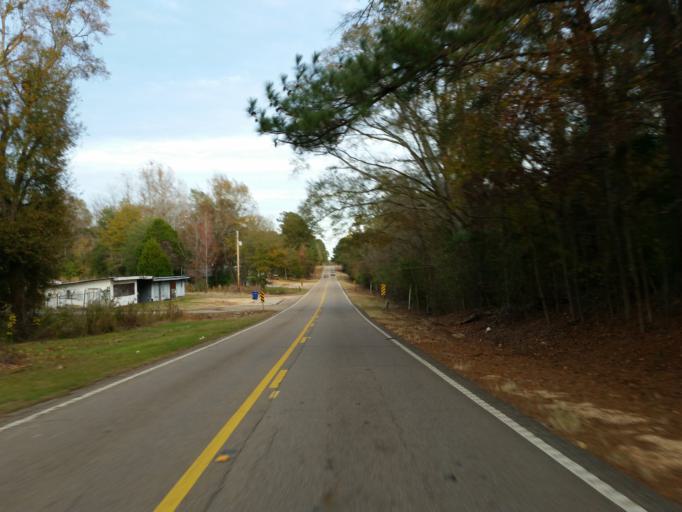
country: US
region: Mississippi
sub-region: Lauderdale County
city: Marion
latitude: 32.4226
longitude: -88.4800
